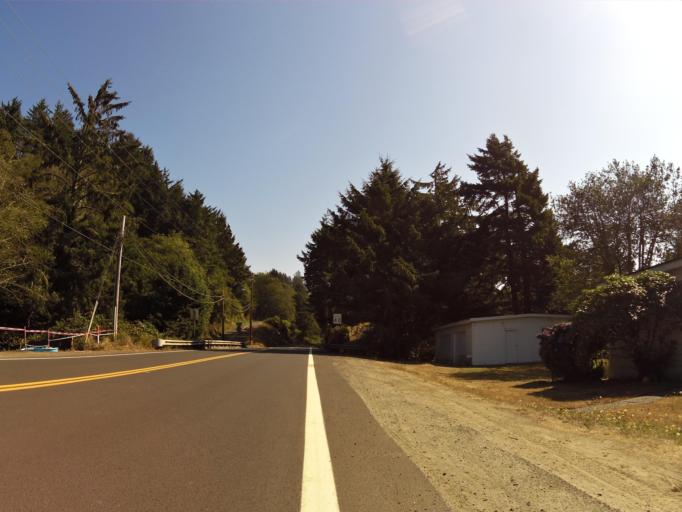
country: US
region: Oregon
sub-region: Tillamook County
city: Pacific City
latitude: 45.1962
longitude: -123.9573
